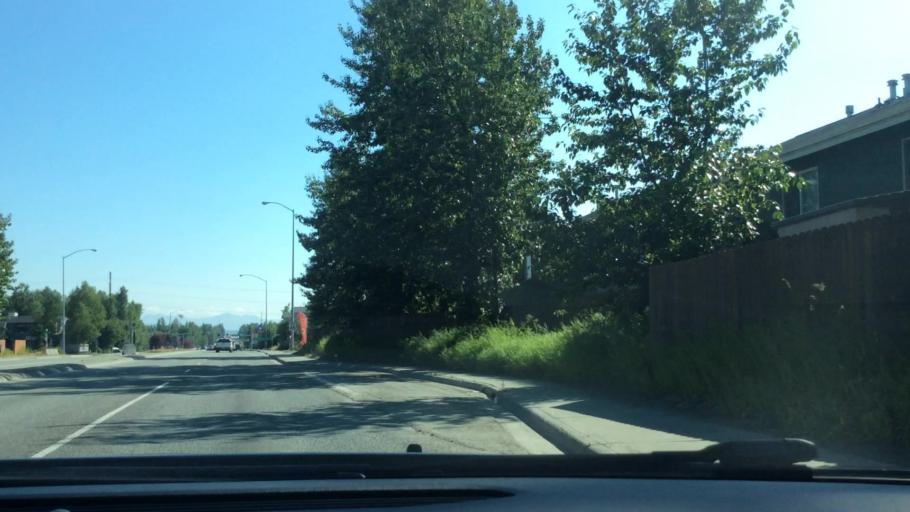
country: US
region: Alaska
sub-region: Anchorage Municipality
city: Anchorage
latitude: 61.1987
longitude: -149.7786
